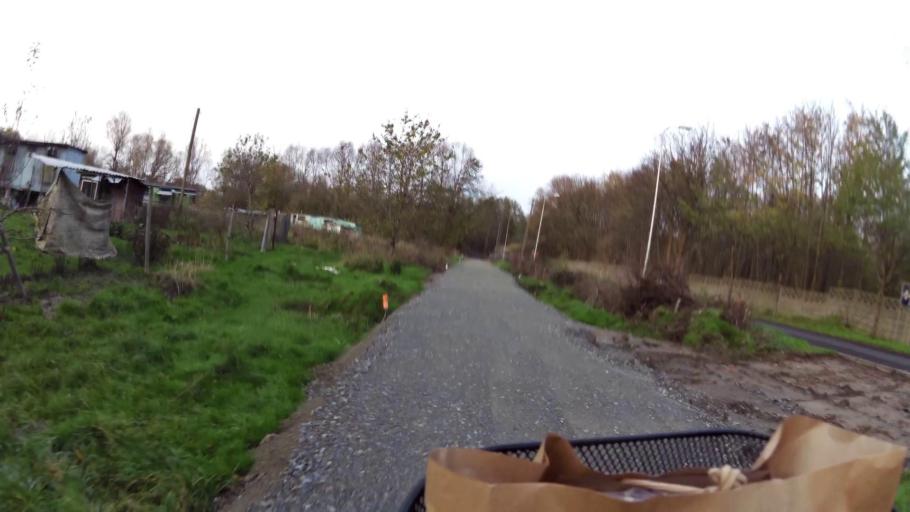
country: PL
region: West Pomeranian Voivodeship
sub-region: Koszalin
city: Koszalin
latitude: 54.2077
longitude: 16.1707
